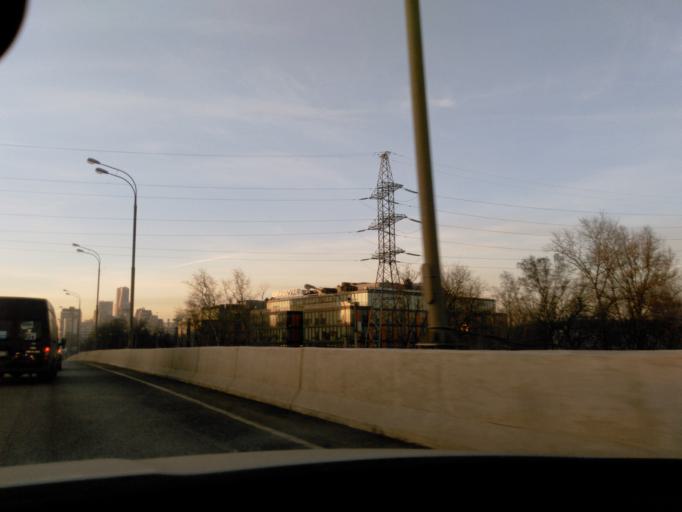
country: RU
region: Moskovskaya
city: Levoberezhnyy
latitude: 55.8394
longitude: 37.4811
